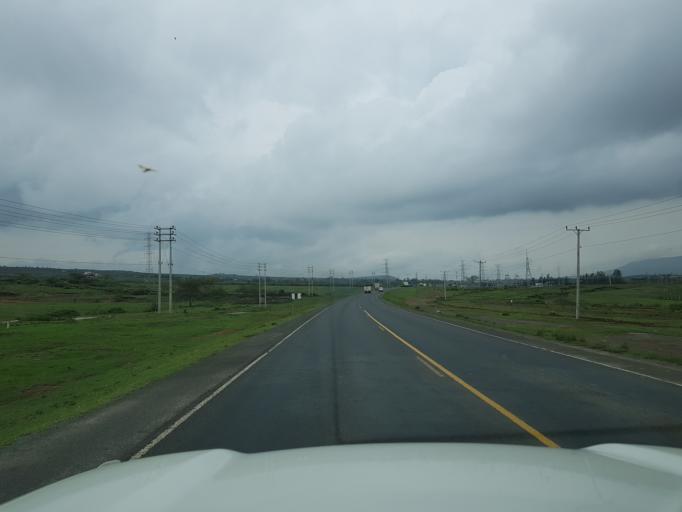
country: KE
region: Nakuru
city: Naivasha
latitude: -0.7918
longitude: 36.4600
